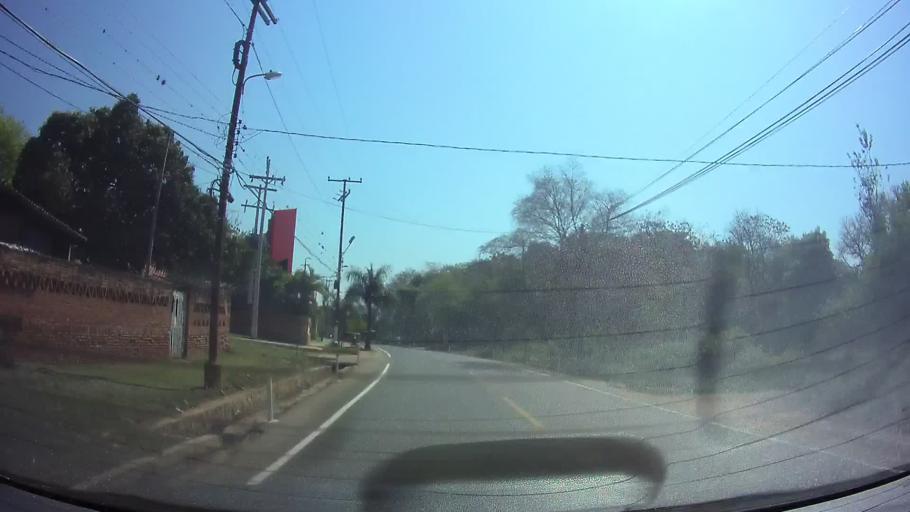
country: PY
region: Central
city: Limpio
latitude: -25.2375
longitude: -57.5057
